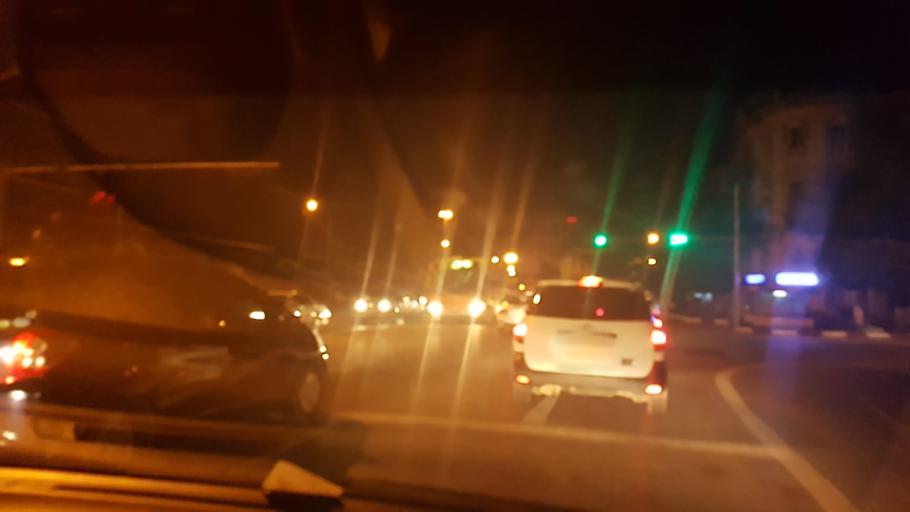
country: MM
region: Yangon
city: Yangon
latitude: 16.7704
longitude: 96.1588
